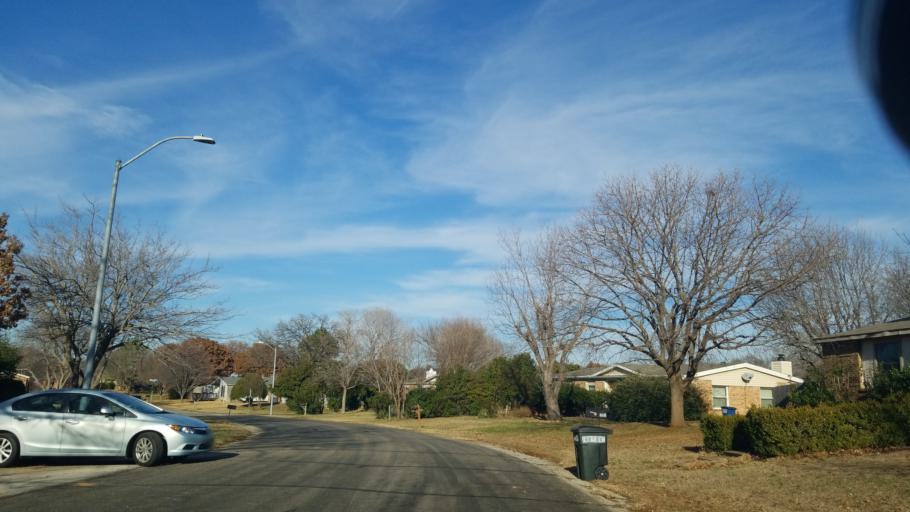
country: US
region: Texas
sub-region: Denton County
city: Corinth
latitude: 33.1367
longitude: -97.0610
